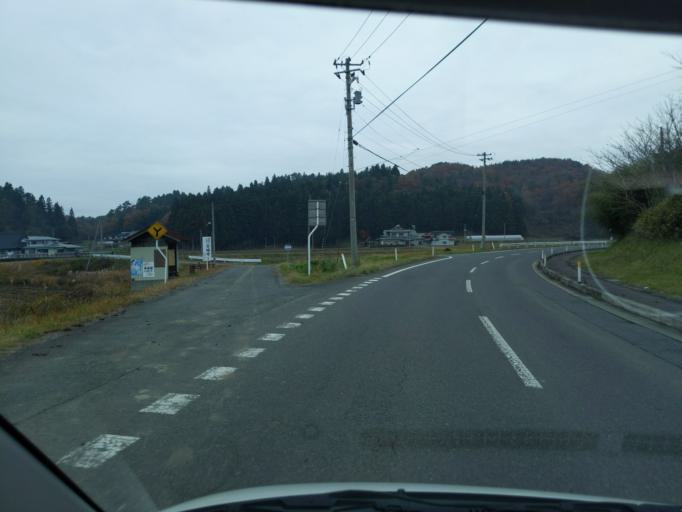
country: JP
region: Iwate
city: Mizusawa
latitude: 39.1783
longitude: 141.2163
